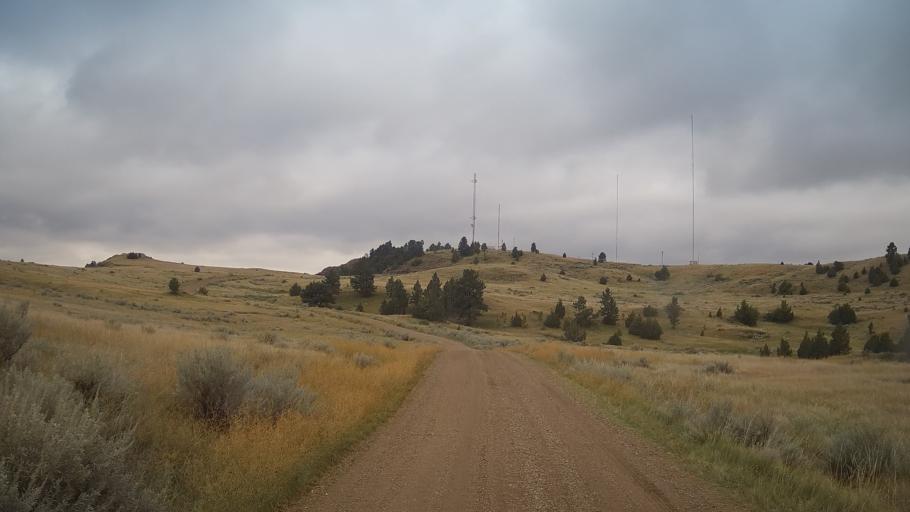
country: US
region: Montana
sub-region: Dawson County
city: Glendive
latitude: 47.0570
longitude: -104.6714
